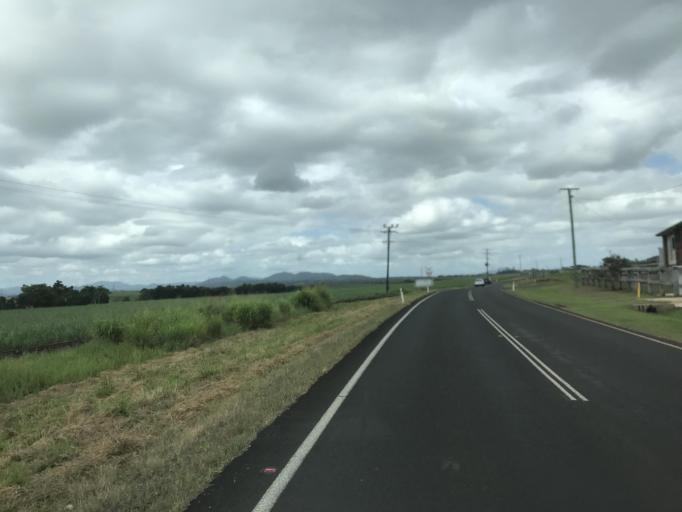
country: AU
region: Queensland
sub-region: Cassowary Coast
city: Innisfail
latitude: -17.5803
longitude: 146.0016
